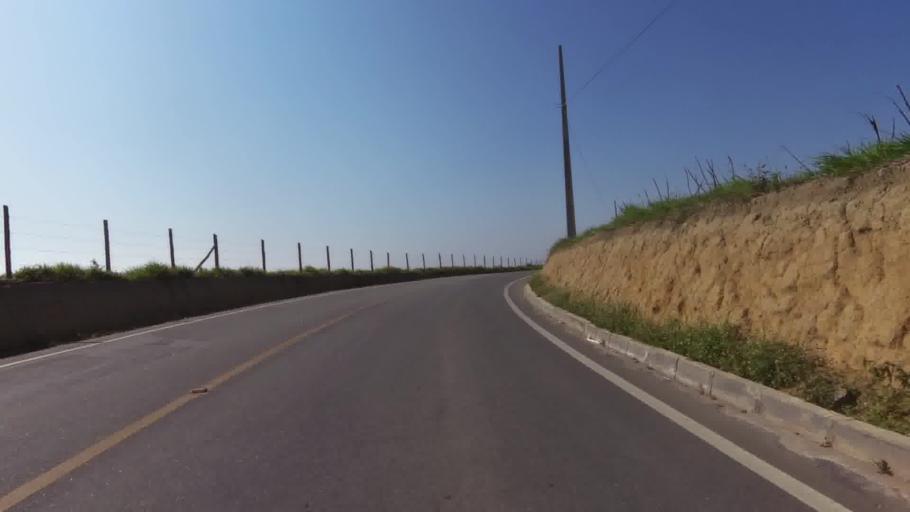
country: BR
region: Espirito Santo
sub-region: Marataizes
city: Marataizes
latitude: -21.0388
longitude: -40.8438
